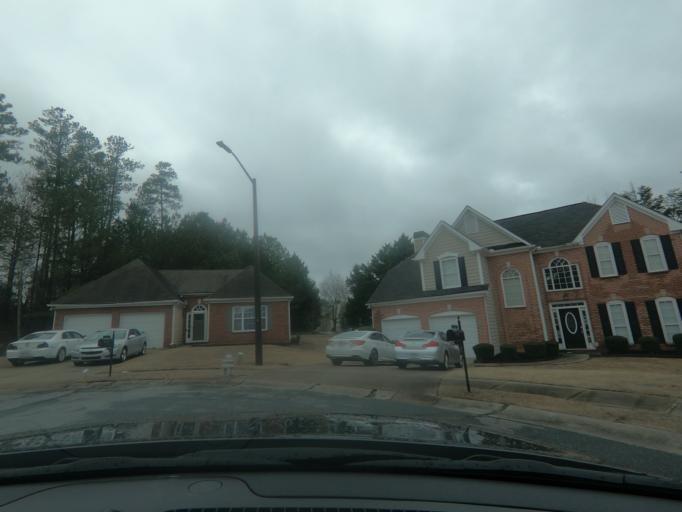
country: US
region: Georgia
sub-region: Cobb County
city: Kennesaw
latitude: 34.0493
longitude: -84.6403
